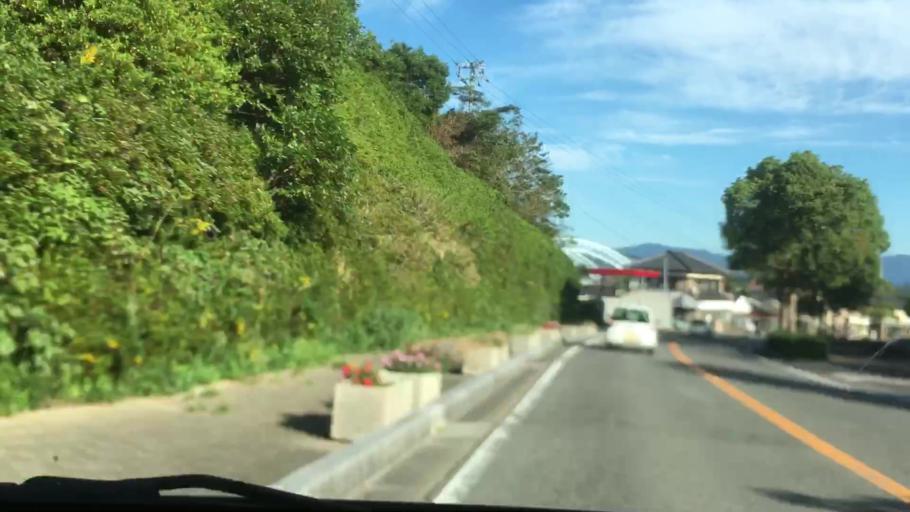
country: JP
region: Nagasaki
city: Sasebo
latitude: 33.0500
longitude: 129.7557
